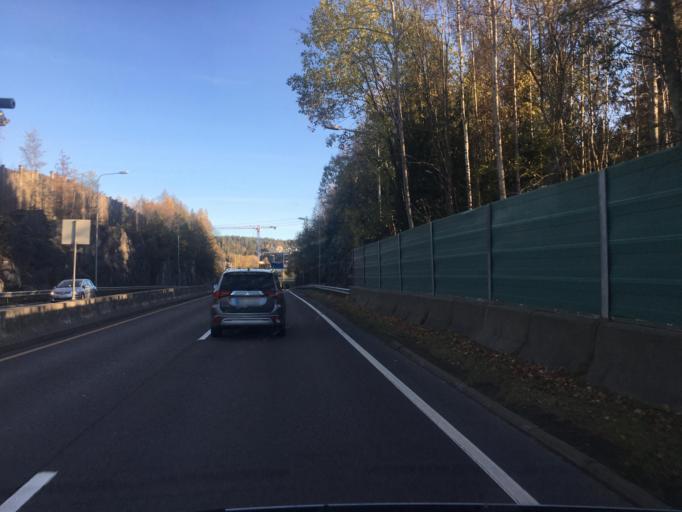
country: NO
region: Akershus
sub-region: Lorenskog
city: Kjenn
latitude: 59.9494
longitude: 10.9420
